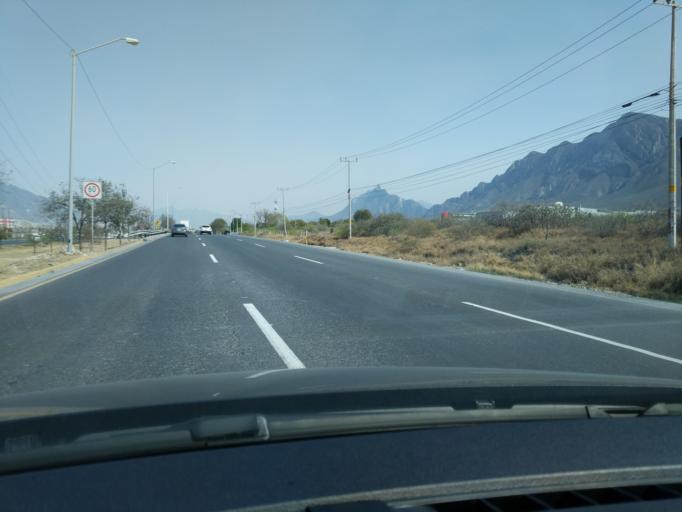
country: MX
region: Nuevo Leon
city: Santa Catarina
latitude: 25.6921
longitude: -100.5088
